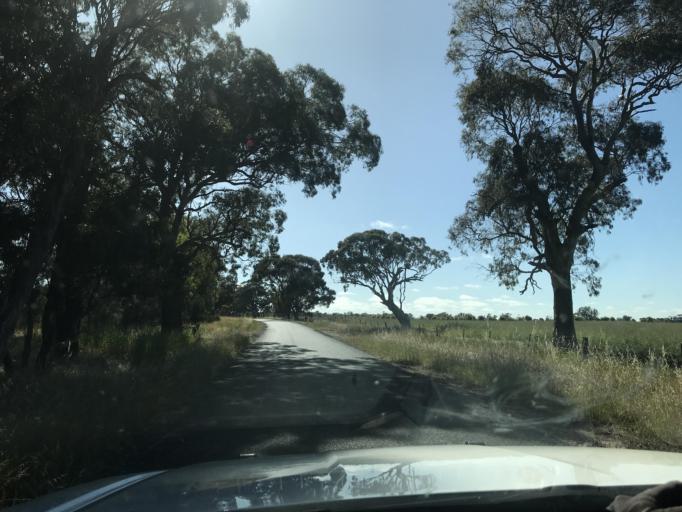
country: AU
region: Victoria
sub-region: Horsham
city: Horsham
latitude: -37.0405
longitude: 141.7342
